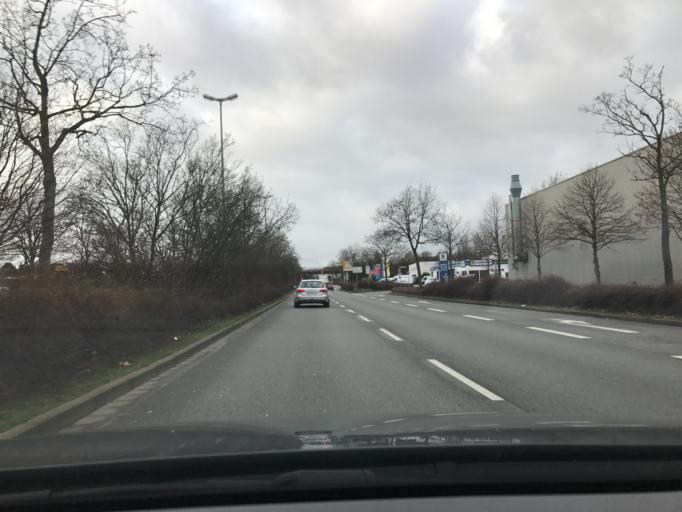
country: DE
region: North Rhine-Westphalia
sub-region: Regierungsbezirk Dusseldorf
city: Krefeld
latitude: 51.3213
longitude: 6.5898
